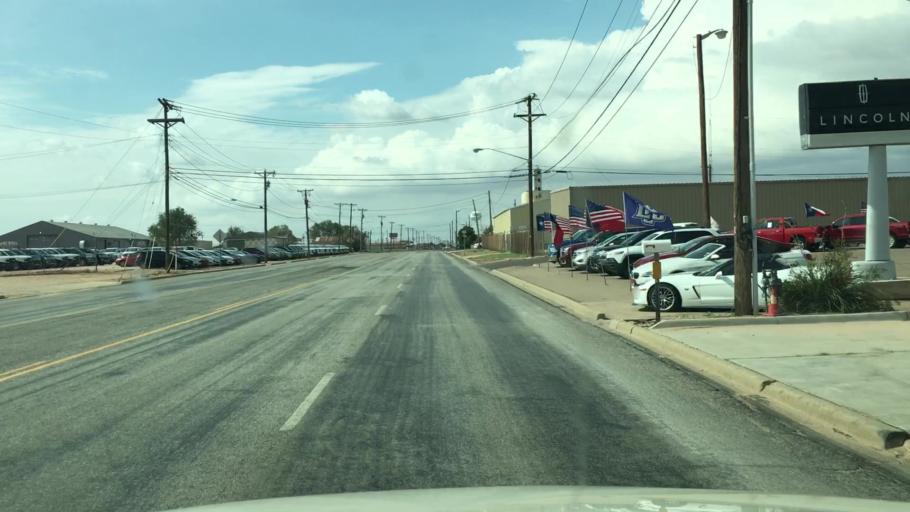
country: US
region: Texas
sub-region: Dawson County
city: Lamesa
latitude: 32.7218
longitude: -101.9456
